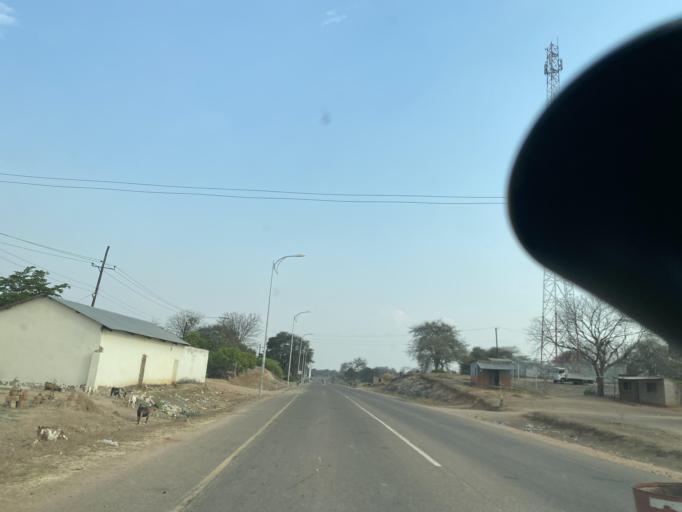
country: ZW
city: Chirundu
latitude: -15.9424
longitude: 28.8743
